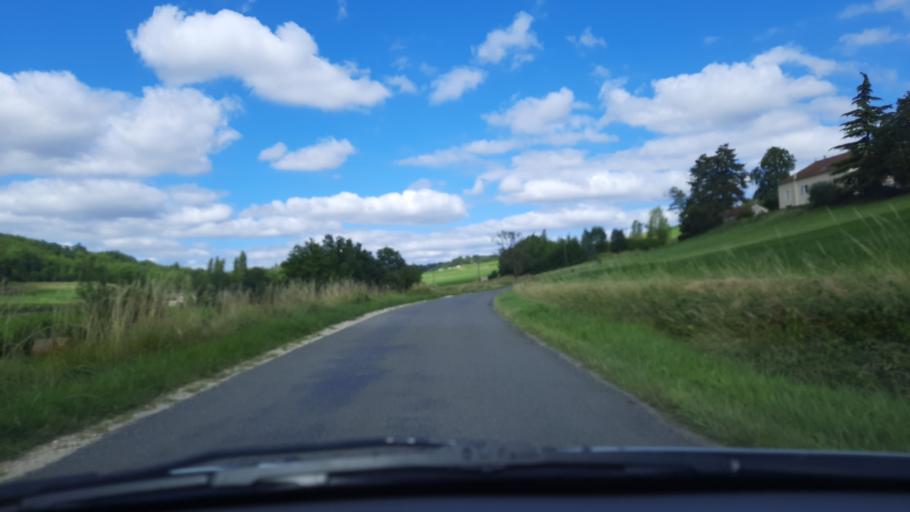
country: FR
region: Midi-Pyrenees
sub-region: Departement du Lot
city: Castelnau-Montratier
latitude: 44.2880
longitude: 1.4262
